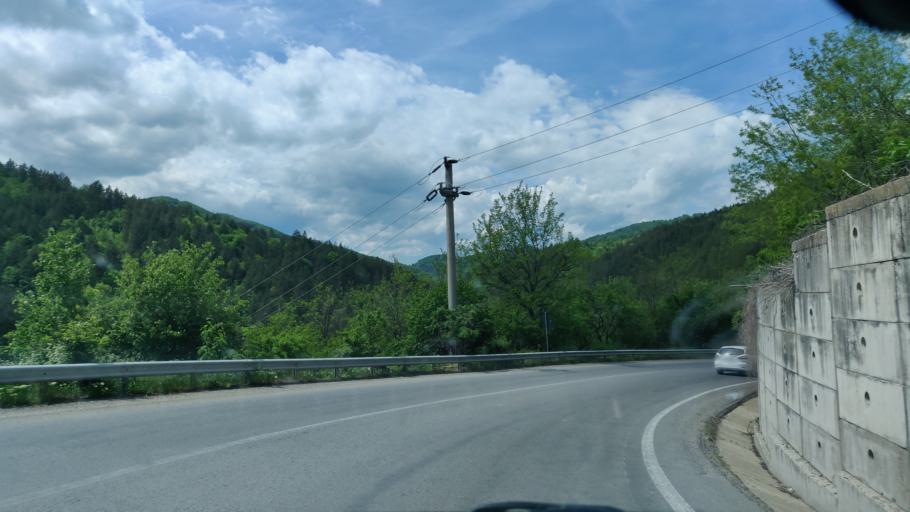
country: RO
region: Vrancea
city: Matacina
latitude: 45.8884
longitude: 26.8144
